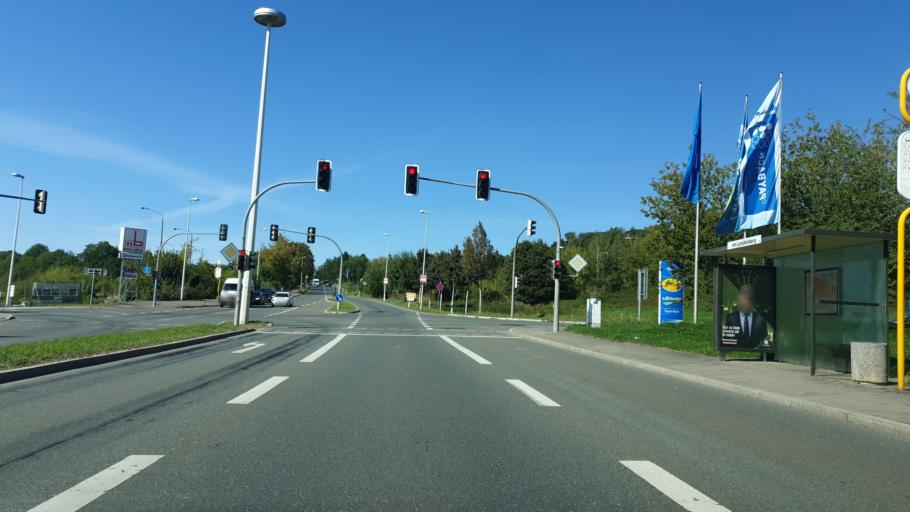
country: DE
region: Thuringia
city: Gera
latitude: 50.9119
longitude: 12.0645
